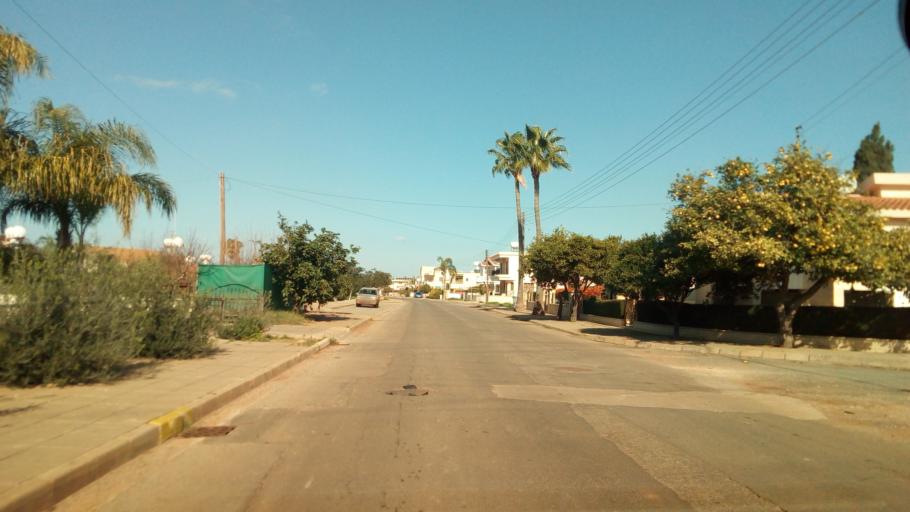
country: CY
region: Ammochostos
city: Avgorou
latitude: 35.0257
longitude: 33.8398
